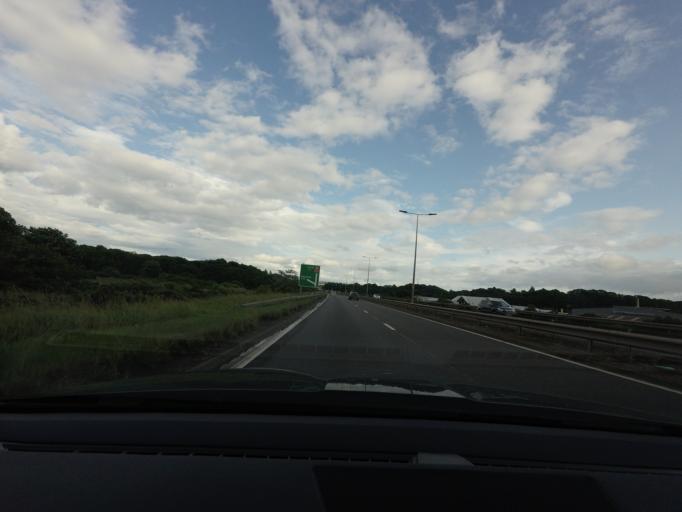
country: GB
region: Scotland
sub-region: Highland
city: Inverness
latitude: 57.4866
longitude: -4.2058
